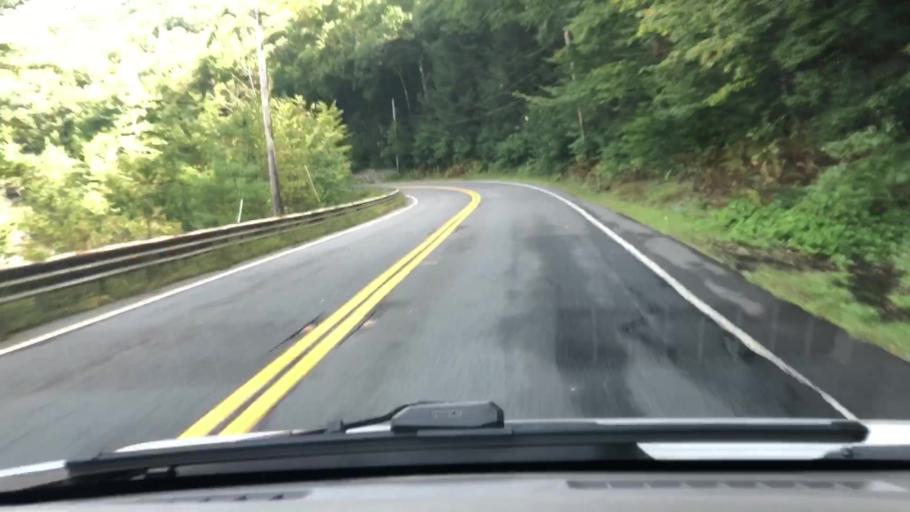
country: US
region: Massachusetts
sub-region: Franklin County
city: Charlemont
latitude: 42.6344
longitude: -72.9280
